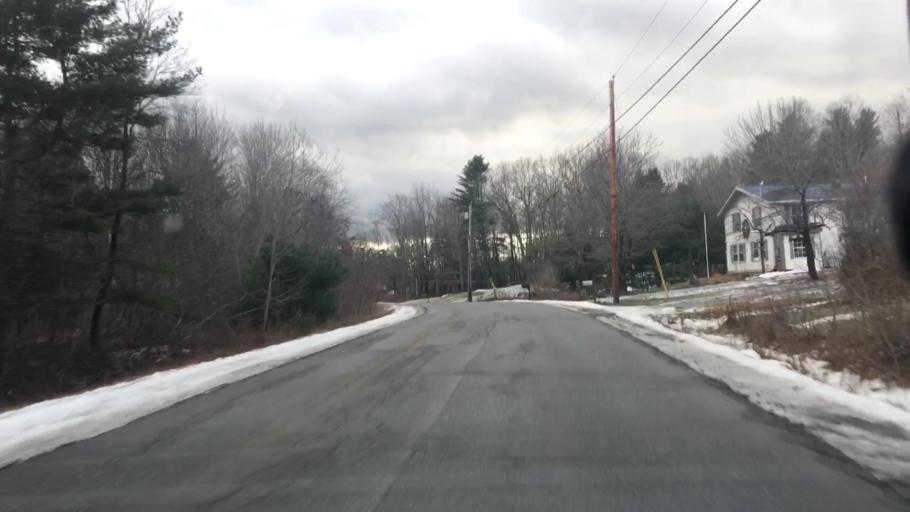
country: US
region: Maine
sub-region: Hancock County
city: Dedham
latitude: 44.6407
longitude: -68.7043
